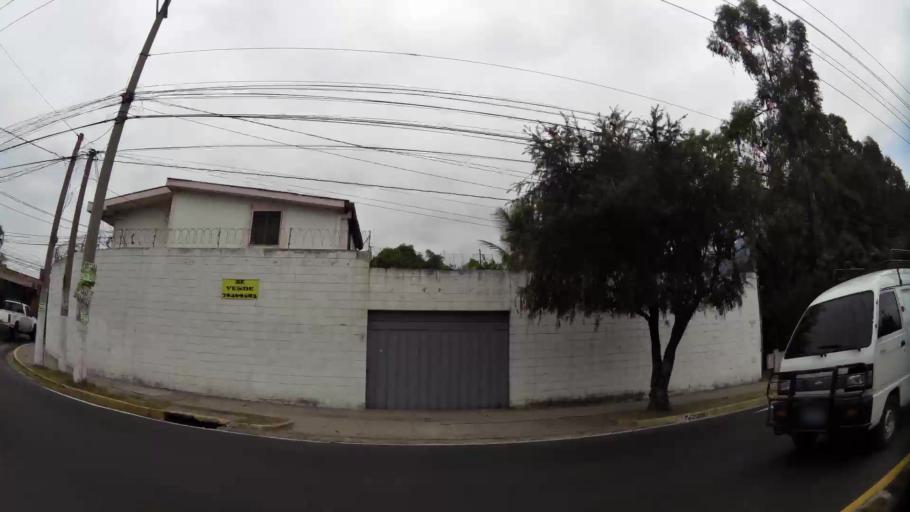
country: SV
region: San Salvador
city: Mejicanos
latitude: 13.7082
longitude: -89.2323
